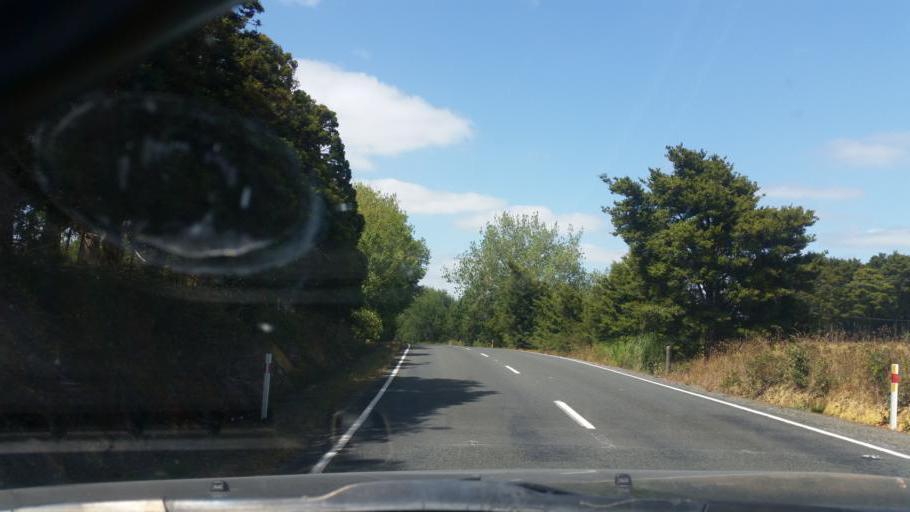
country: NZ
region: Northland
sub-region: Whangarei
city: Ruakaka
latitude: -35.9901
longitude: 174.2930
